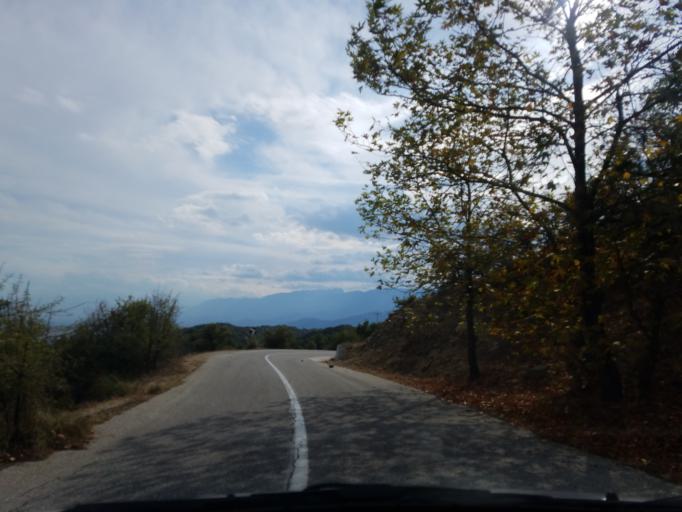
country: GR
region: Thessaly
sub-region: Trikala
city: Kastraki
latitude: 39.7441
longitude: 21.6582
